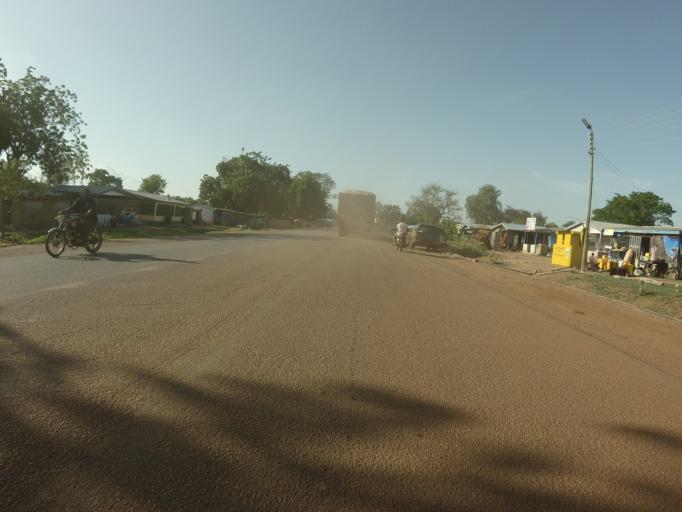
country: GH
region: Upper East
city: Navrongo
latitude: 10.9054
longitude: -1.0912
